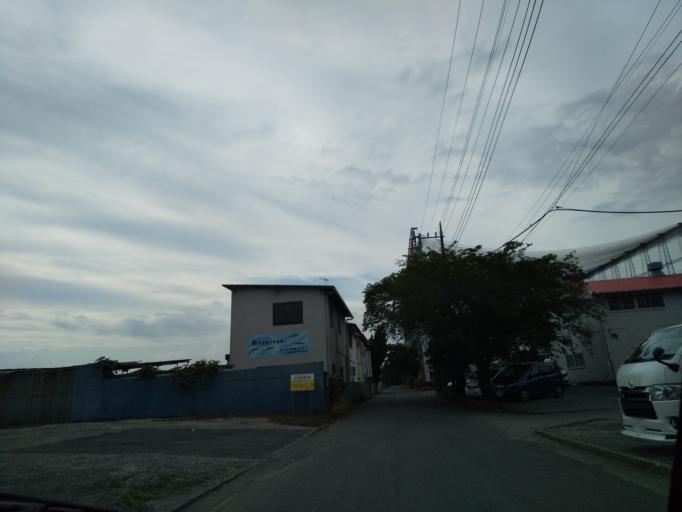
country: JP
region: Kanagawa
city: Zama
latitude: 35.4723
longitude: 139.3611
